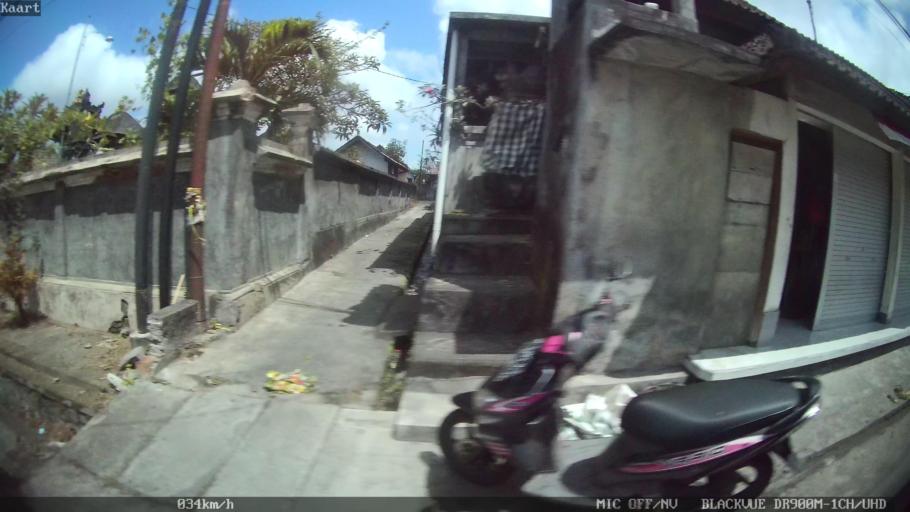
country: ID
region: Bali
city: Banjar Pasekan
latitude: -8.5907
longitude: 115.2968
